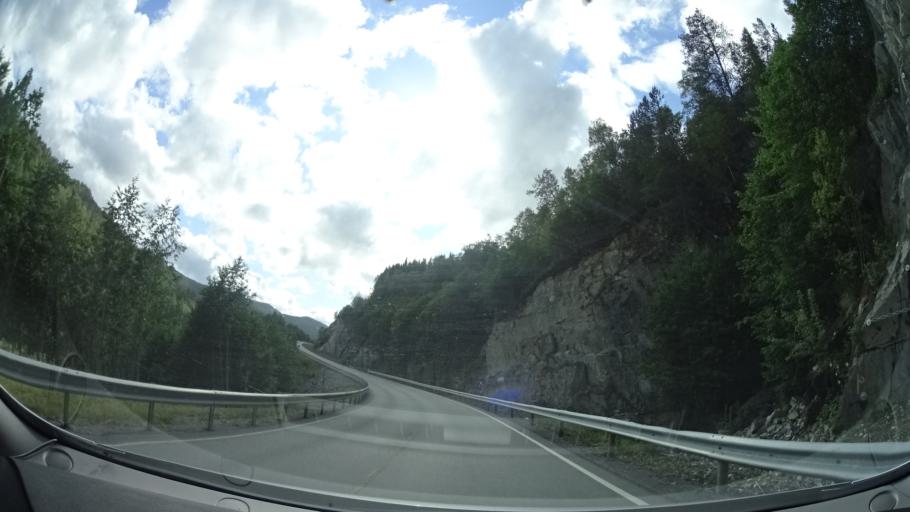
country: NO
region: Sor-Trondelag
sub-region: Hemne
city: Kyrksaeterora
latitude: 63.2168
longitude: 9.1181
